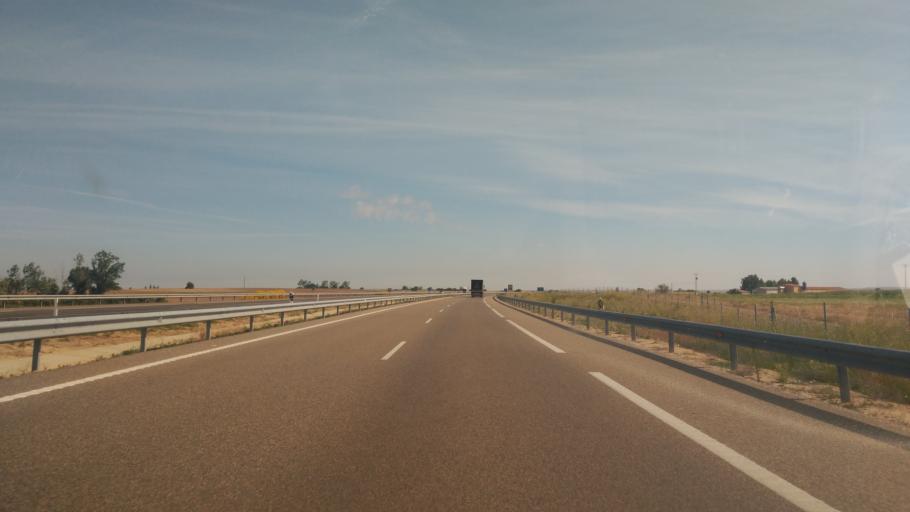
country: ES
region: Castille and Leon
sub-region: Provincia de Zamora
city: Morales del Vino
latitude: 41.4280
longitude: -5.7225
